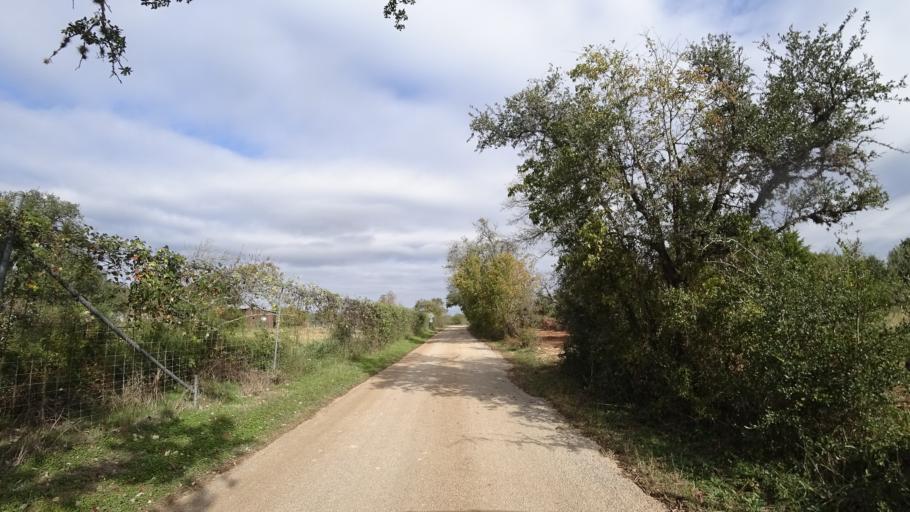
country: US
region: Texas
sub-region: Travis County
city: Shady Hollow
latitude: 30.1371
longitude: -97.8686
